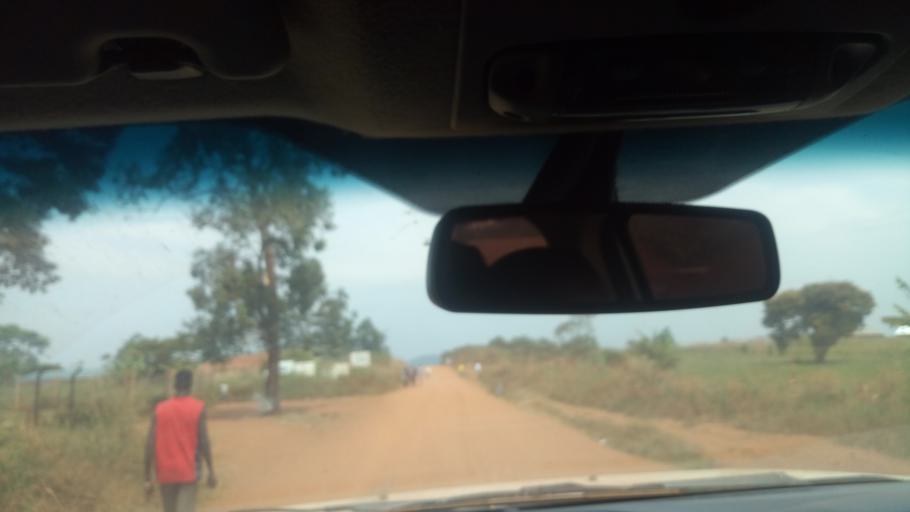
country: UG
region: Western Region
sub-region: Kiryandongo District
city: Kiryandongo
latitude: 1.9395
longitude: 32.1704
